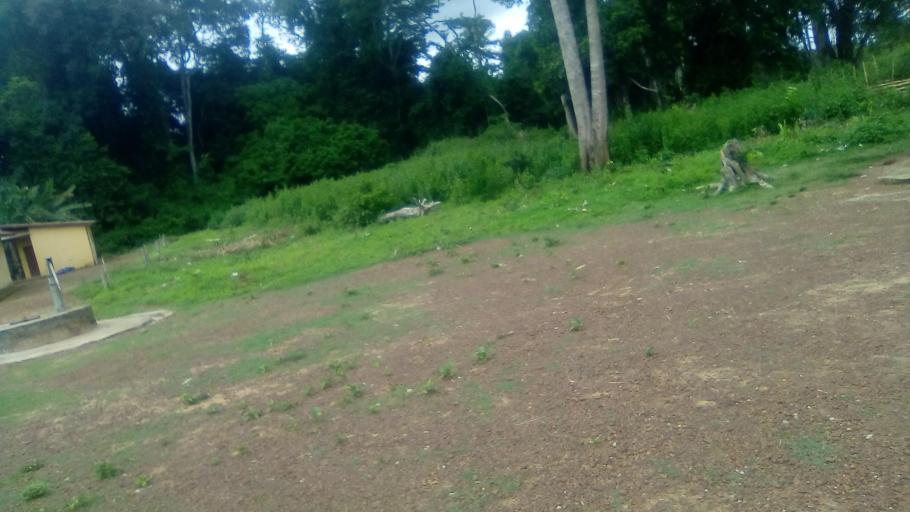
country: SL
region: Southern Province
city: Moyamba
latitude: 8.1364
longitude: -12.4052
